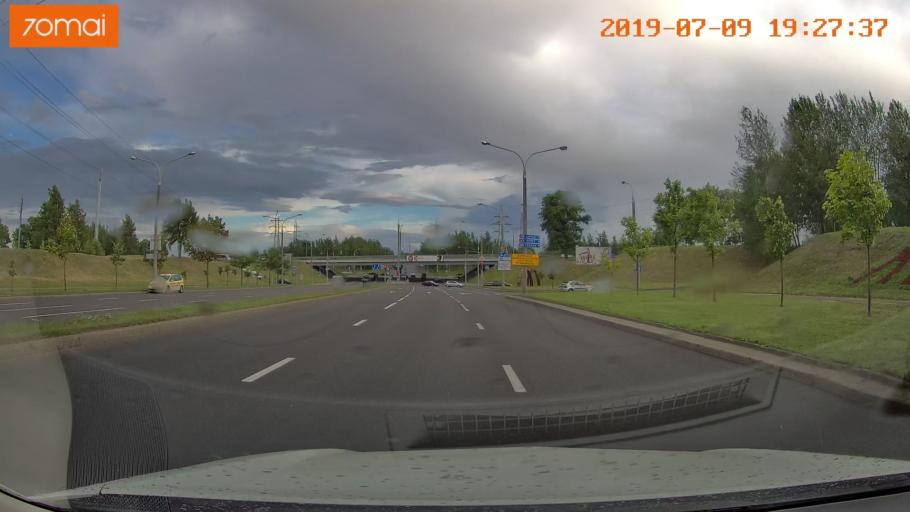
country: BY
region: Minsk
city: Syenitsa
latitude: 53.8347
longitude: 27.5745
